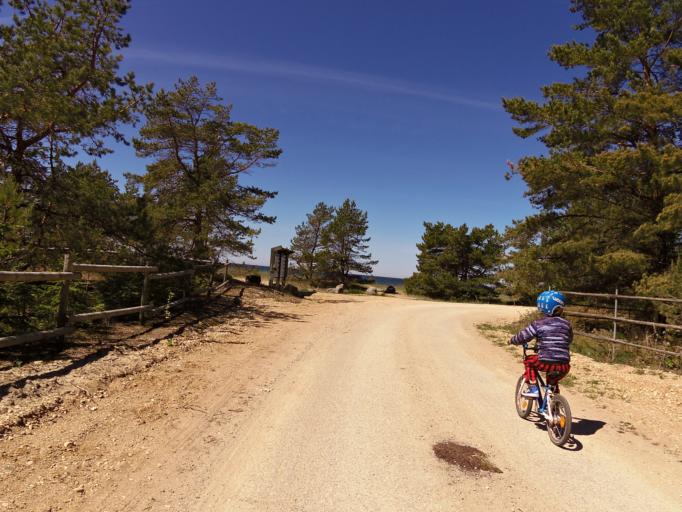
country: EE
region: Harju
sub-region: Paldiski linn
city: Paldiski
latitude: 59.2734
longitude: 23.7790
